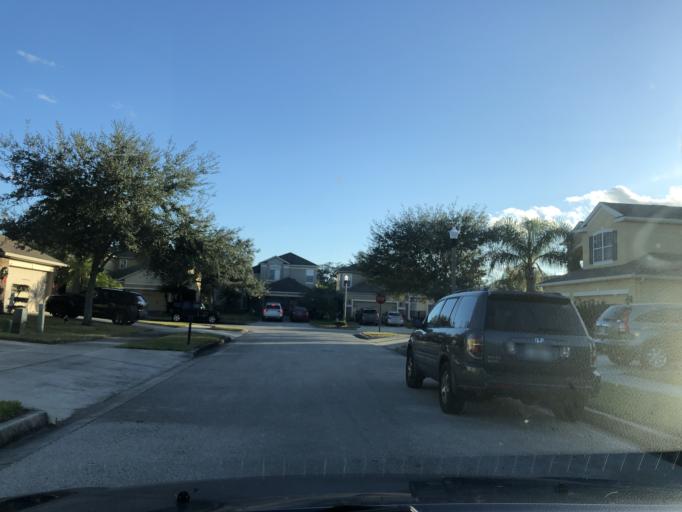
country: US
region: Florida
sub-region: Seminole County
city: Goldenrod
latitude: 28.6137
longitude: -81.2628
